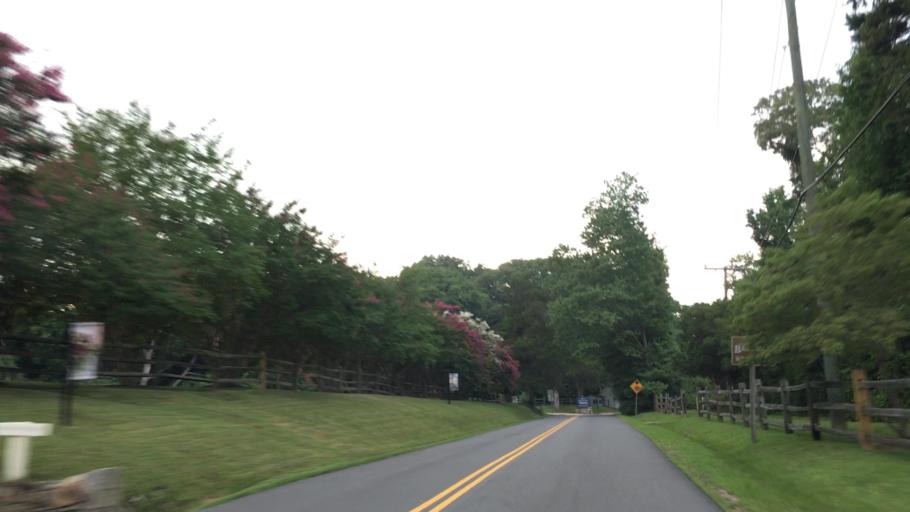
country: US
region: Virginia
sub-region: Stafford County
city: Falmouth
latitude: 38.3246
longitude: -77.4727
